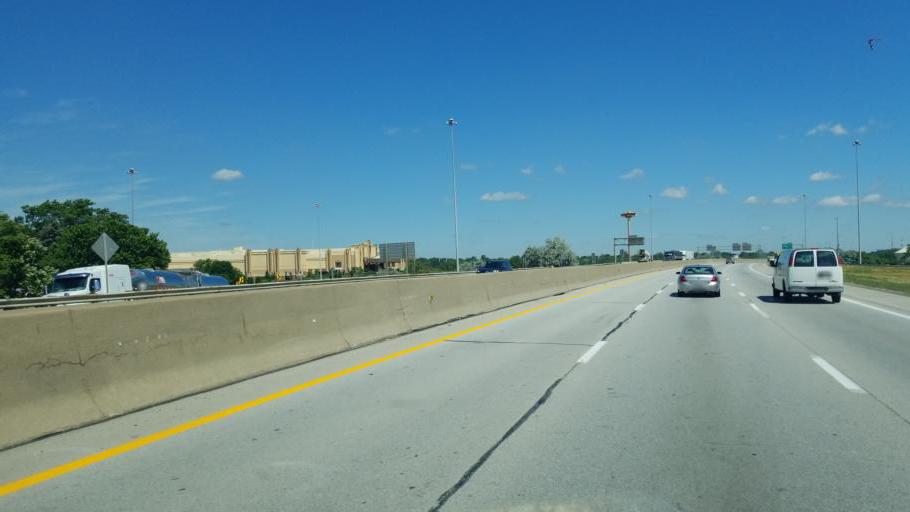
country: US
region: Ohio
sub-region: Wood County
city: Rossford
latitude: 41.6180
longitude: -83.5411
